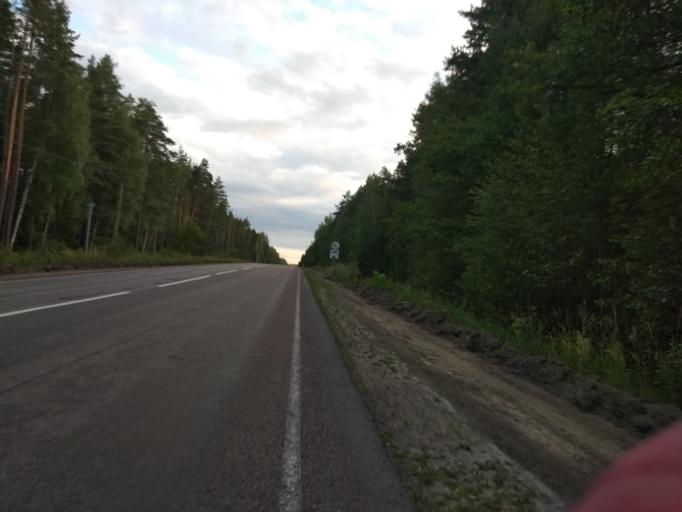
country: RU
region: Moskovskaya
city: Misheronskiy
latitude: 55.6399
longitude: 39.7525
